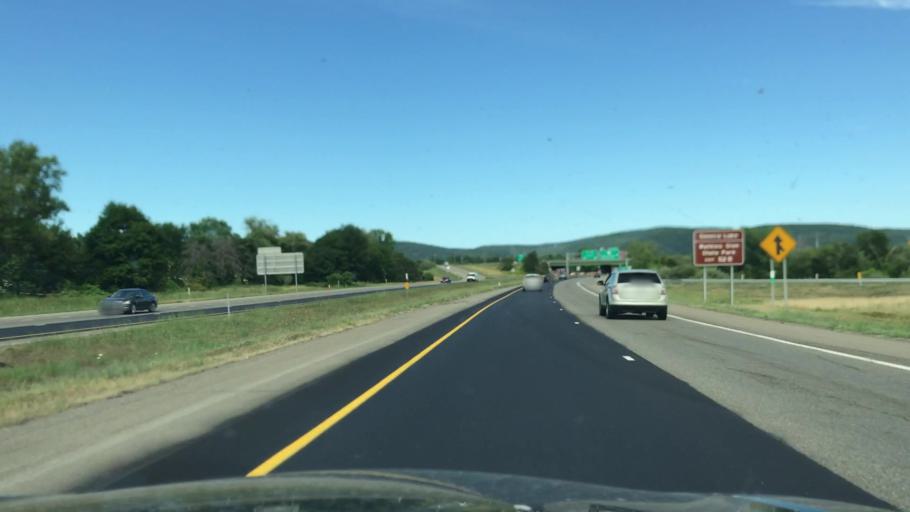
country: US
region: New York
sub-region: Chemung County
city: Horseheads
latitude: 42.1614
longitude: -76.8526
